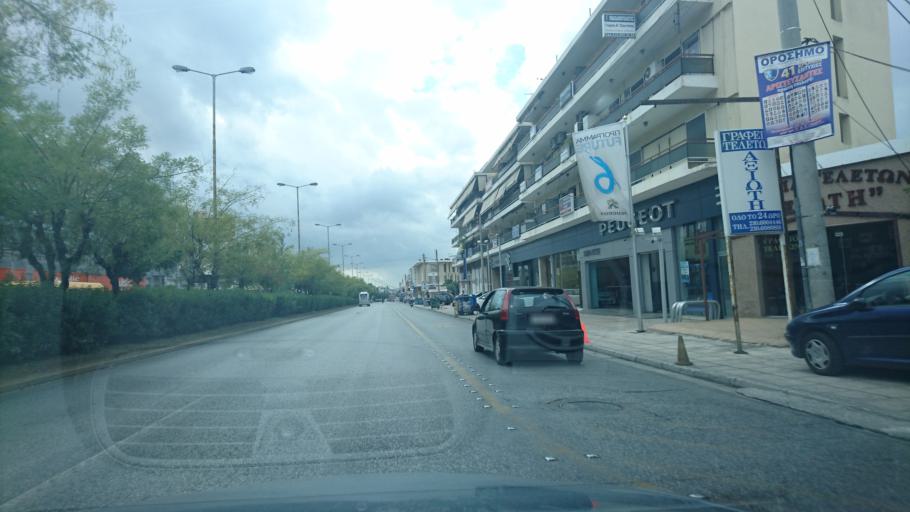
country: GR
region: Attica
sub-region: Nomarchia Athinas
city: Agia Paraskevi
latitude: 38.0133
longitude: 23.8190
